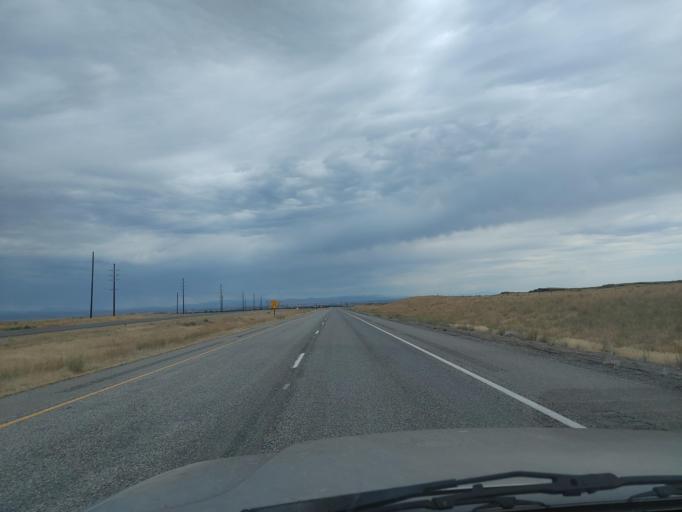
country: US
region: Idaho
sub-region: Lincoln County
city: Shoshone
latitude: 42.8957
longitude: -114.4243
